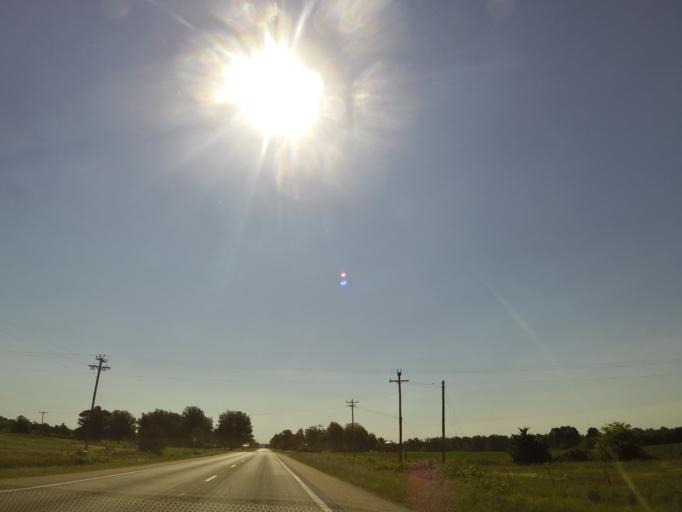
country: US
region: Arkansas
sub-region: Clay County
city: Corning
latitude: 36.4346
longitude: -90.3987
